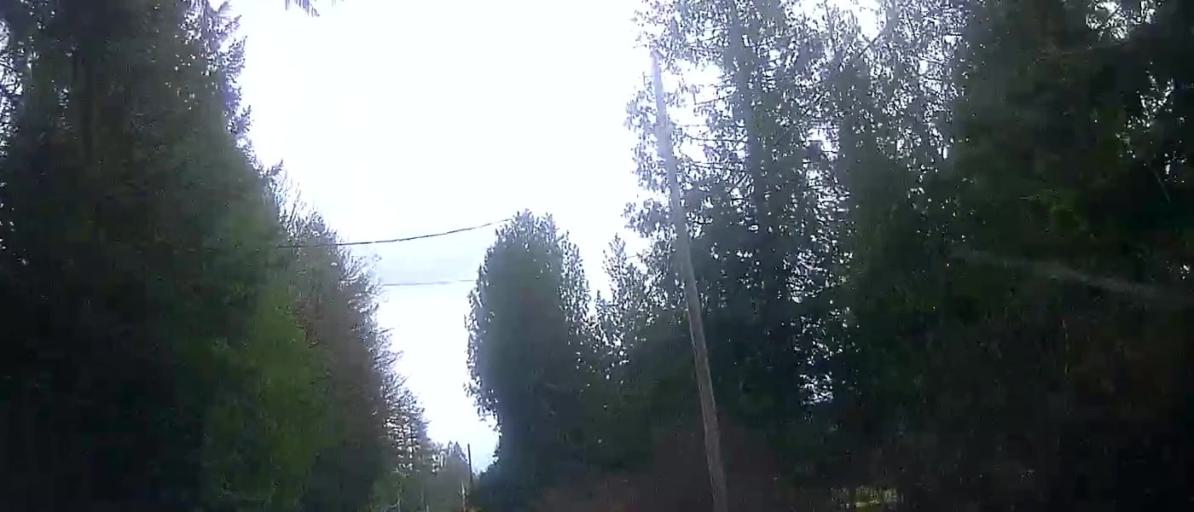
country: US
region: Washington
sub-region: Skagit County
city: Sedro-Woolley
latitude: 48.5636
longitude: -122.2943
